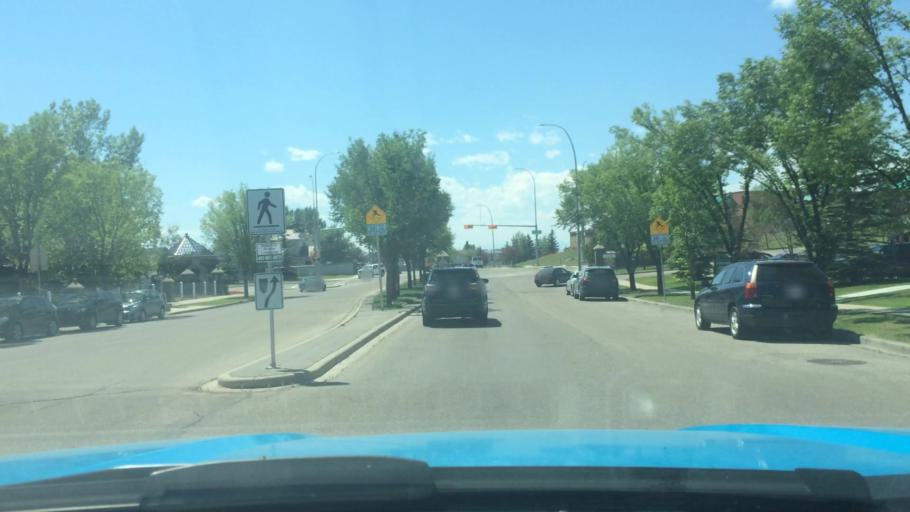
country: CA
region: Alberta
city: Calgary
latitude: 51.1338
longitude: -114.2030
